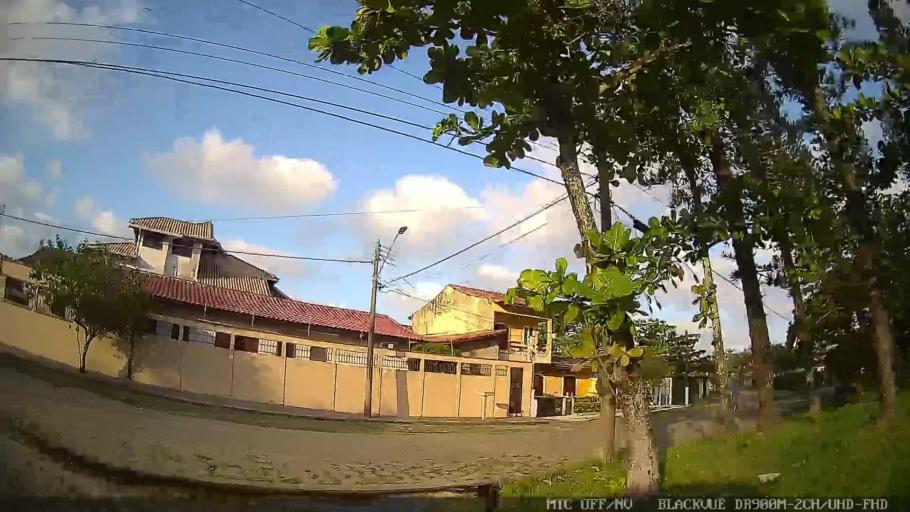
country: BR
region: Sao Paulo
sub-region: Peruibe
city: Peruibe
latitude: -24.3186
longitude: -46.9915
